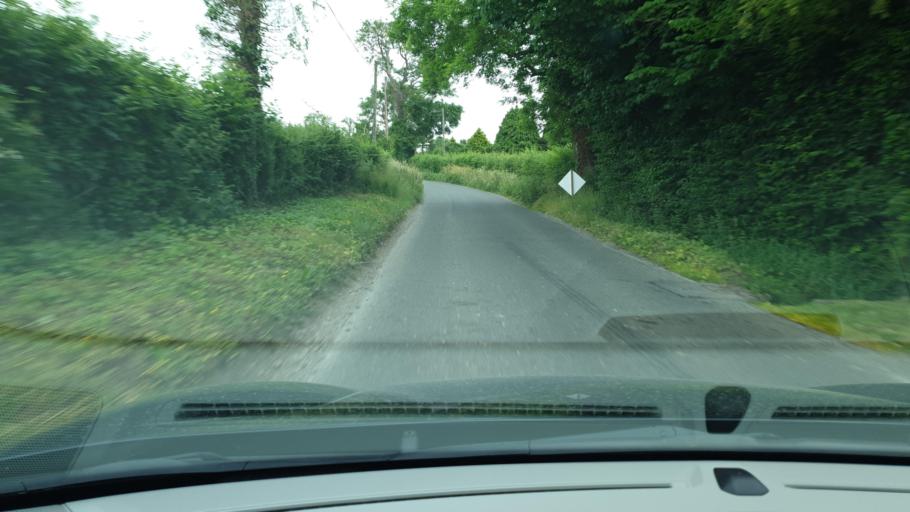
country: IE
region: Leinster
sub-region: An Mhi
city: Ashbourne
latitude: 53.4767
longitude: -6.3749
